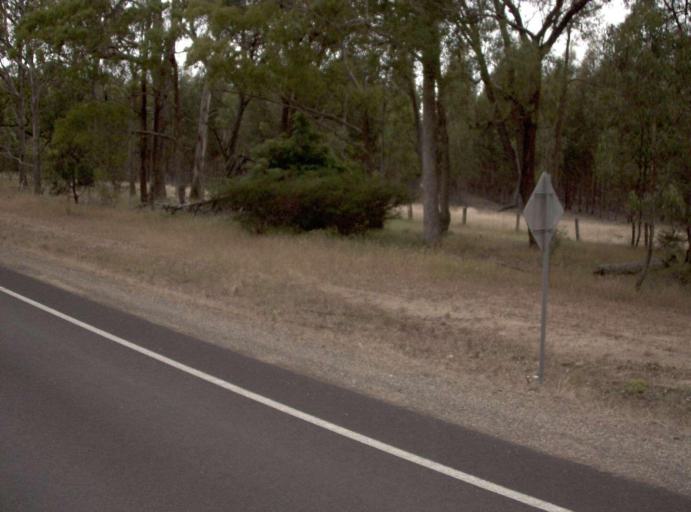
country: AU
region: Victoria
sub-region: Wellington
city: Sale
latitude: -38.4300
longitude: 146.9525
